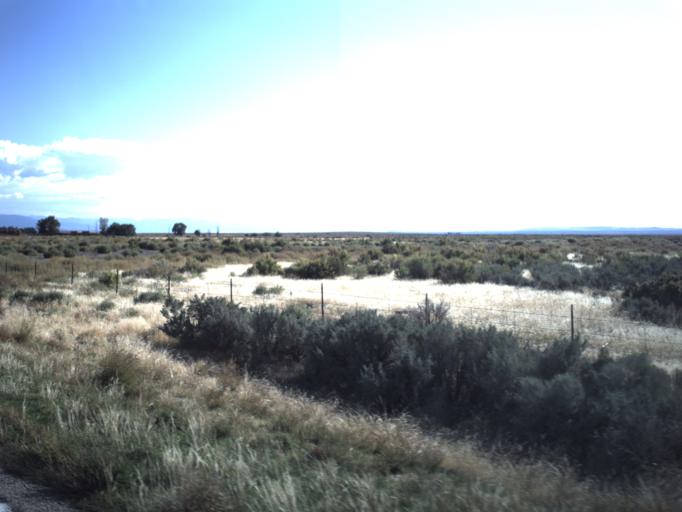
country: US
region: Utah
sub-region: Millard County
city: Delta
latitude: 39.2201
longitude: -112.4203
